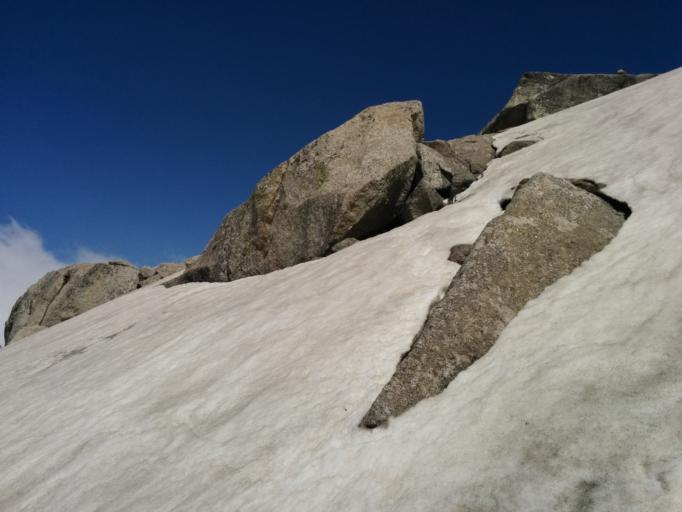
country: IN
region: Himachal Pradesh
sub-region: Kangra
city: Dharmsala
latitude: 32.2897
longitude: 76.3743
